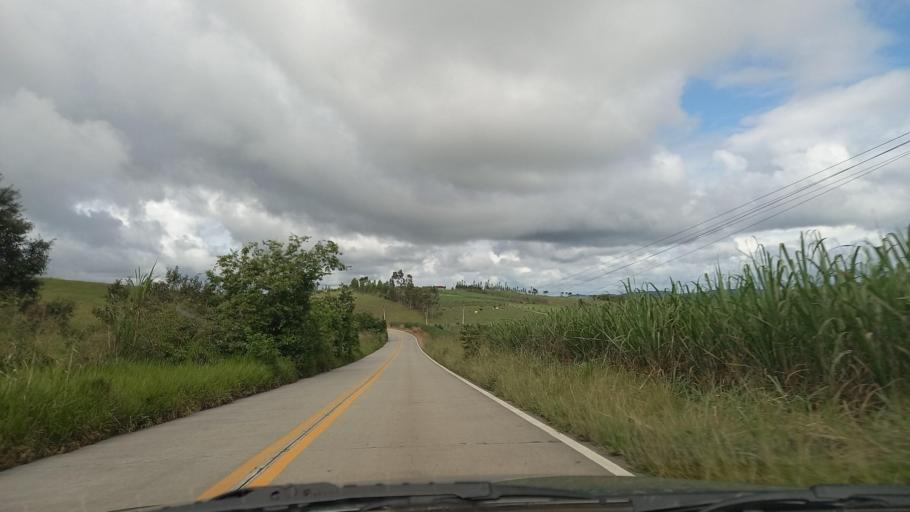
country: BR
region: Pernambuco
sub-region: Quipapa
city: Quipapa
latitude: -8.7793
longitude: -35.9390
